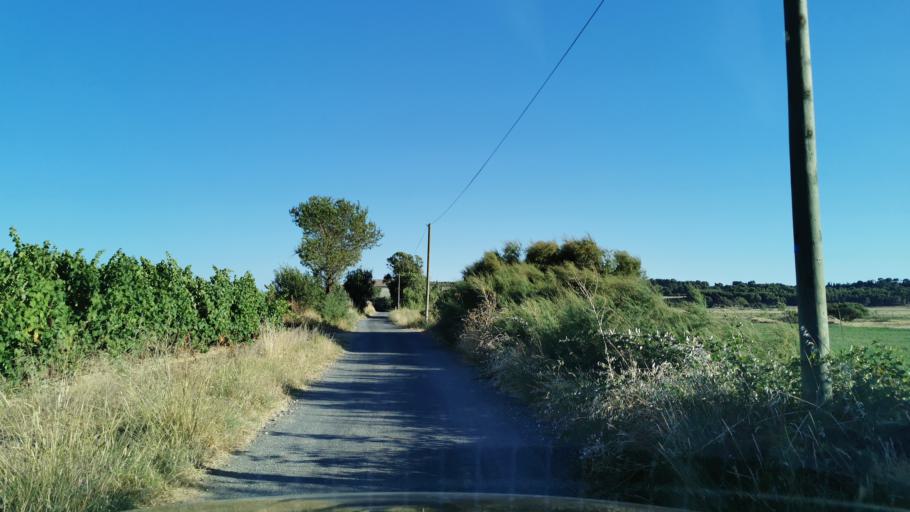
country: FR
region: Languedoc-Roussillon
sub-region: Departement de l'Aude
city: Ouveillan
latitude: 43.2809
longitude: 2.9759
